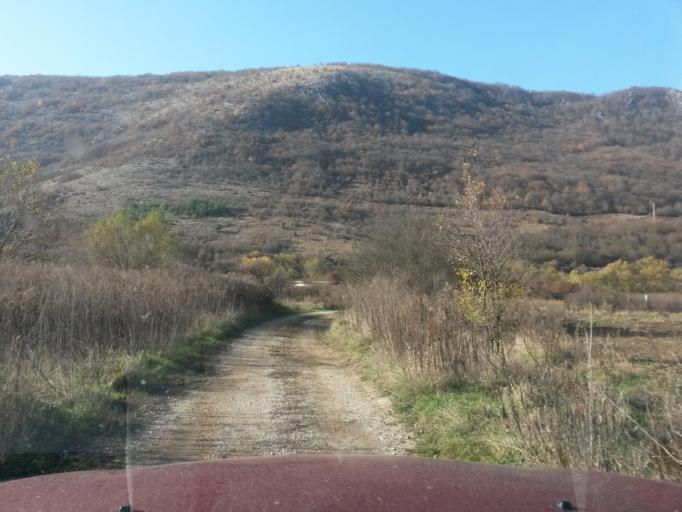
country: SK
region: Kosicky
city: Roznava
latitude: 48.5906
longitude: 20.4740
